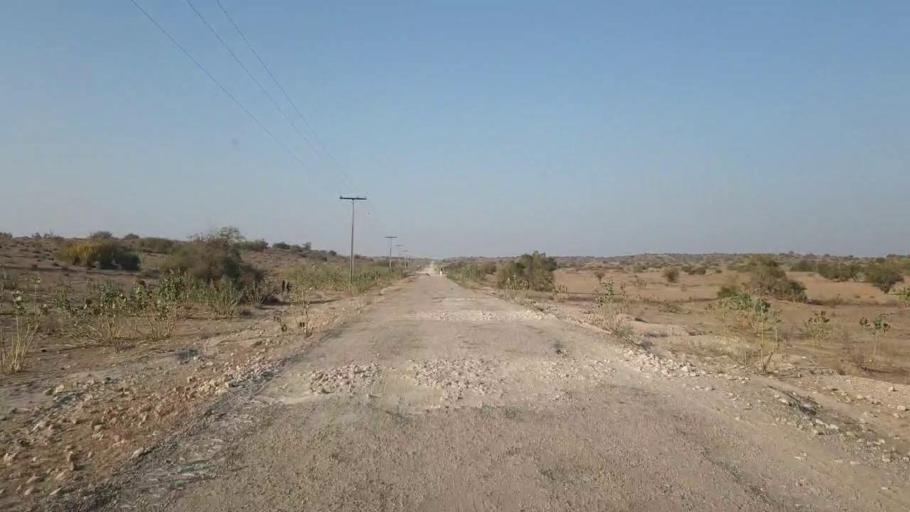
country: PK
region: Sindh
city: Chor
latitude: 25.6117
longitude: 69.8377
